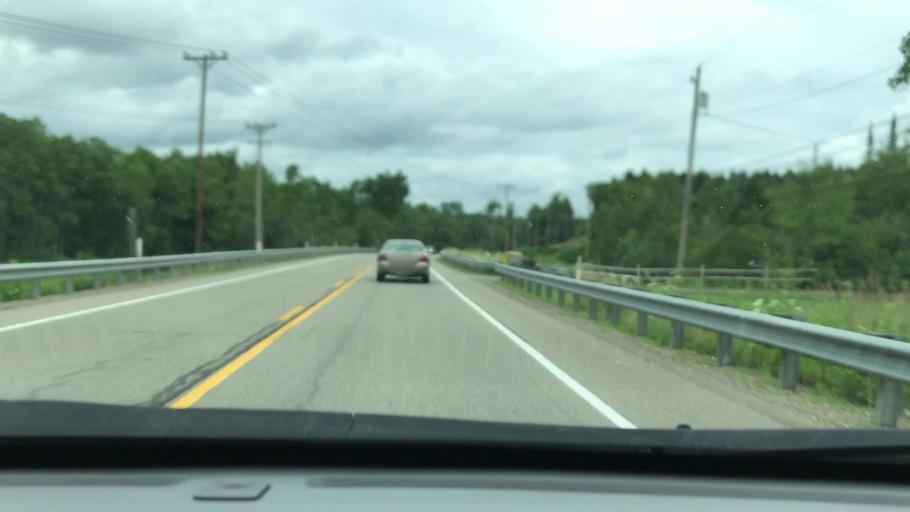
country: US
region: Pennsylvania
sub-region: Elk County
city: Johnsonburg
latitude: 41.5310
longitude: -78.6805
